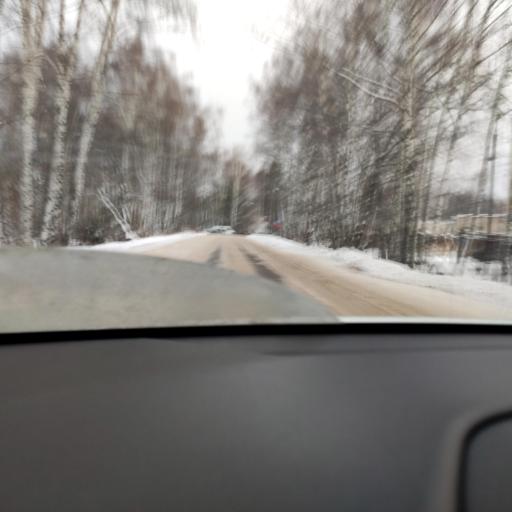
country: RU
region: Tatarstan
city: Osinovo
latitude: 55.8903
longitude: 48.8255
